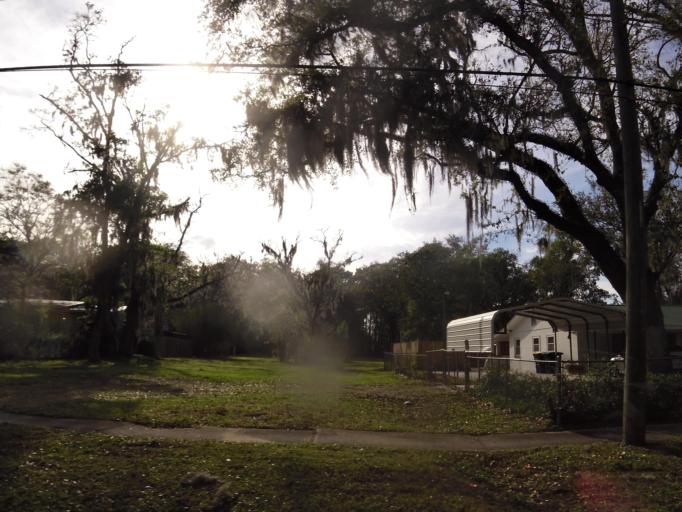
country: US
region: Florida
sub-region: Clay County
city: Bellair-Meadowbrook Terrace
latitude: 30.2400
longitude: -81.7646
